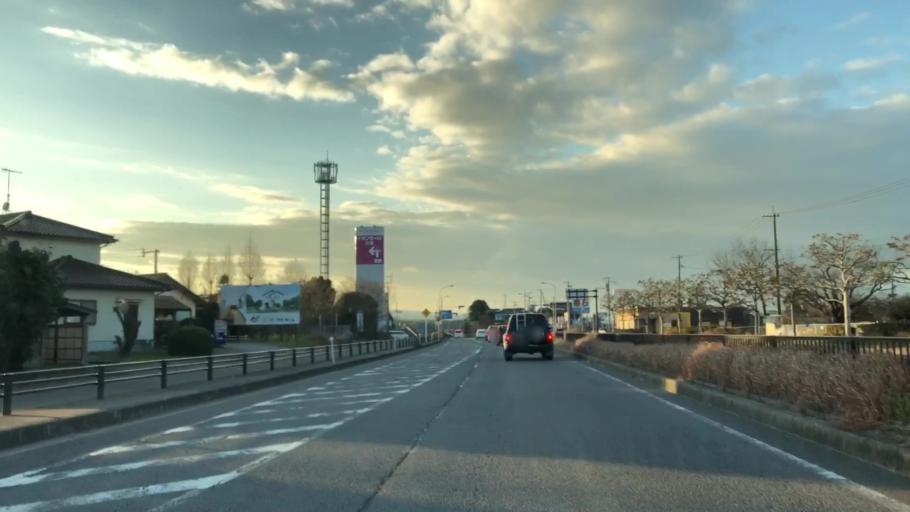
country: JP
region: Fukuoka
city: Nakatsu
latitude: 33.5600
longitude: 131.1966
